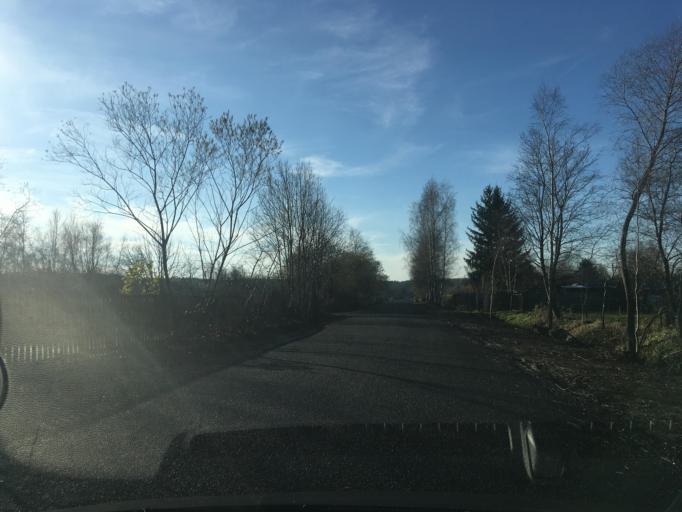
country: EE
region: Harju
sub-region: Maardu linn
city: Maardu
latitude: 59.4759
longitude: 25.0404
